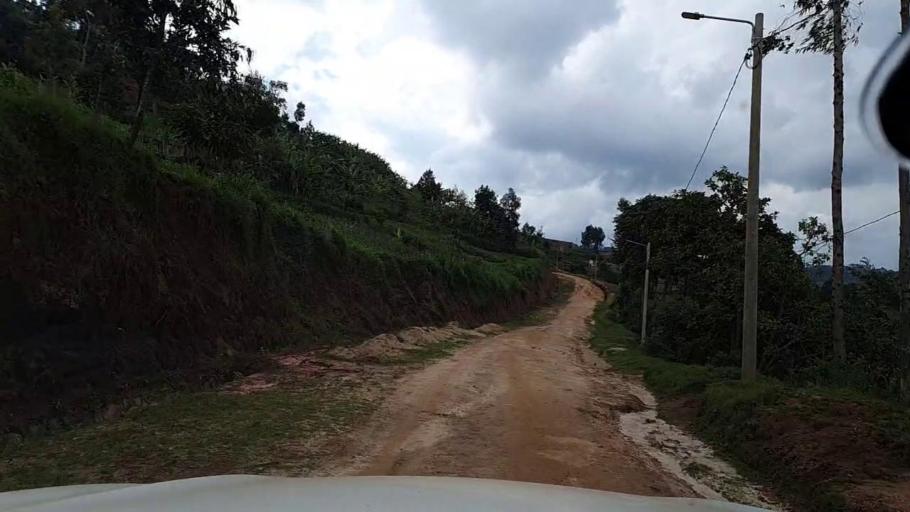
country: RW
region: Southern Province
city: Nzega
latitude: -2.7040
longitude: 29.4306
